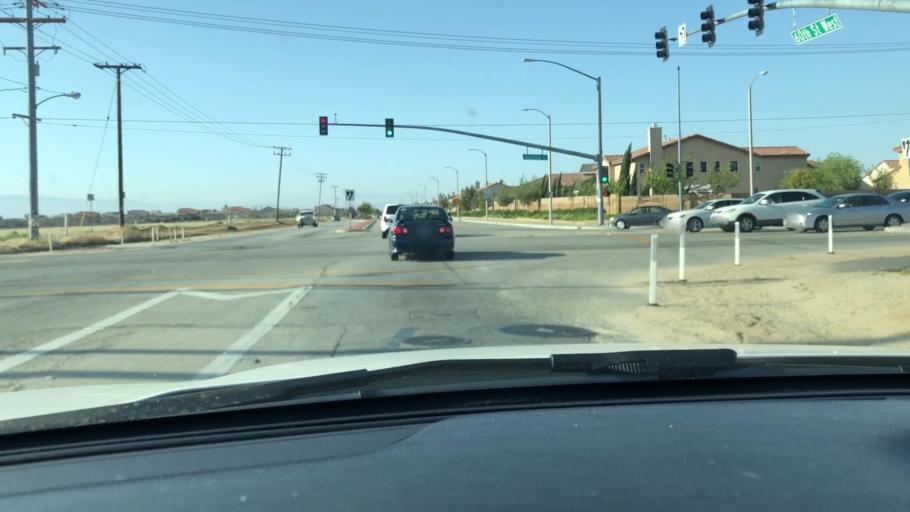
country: US
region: California
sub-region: Los Angeles County
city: Quartz Hill
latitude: 34.6600
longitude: -118.2363
